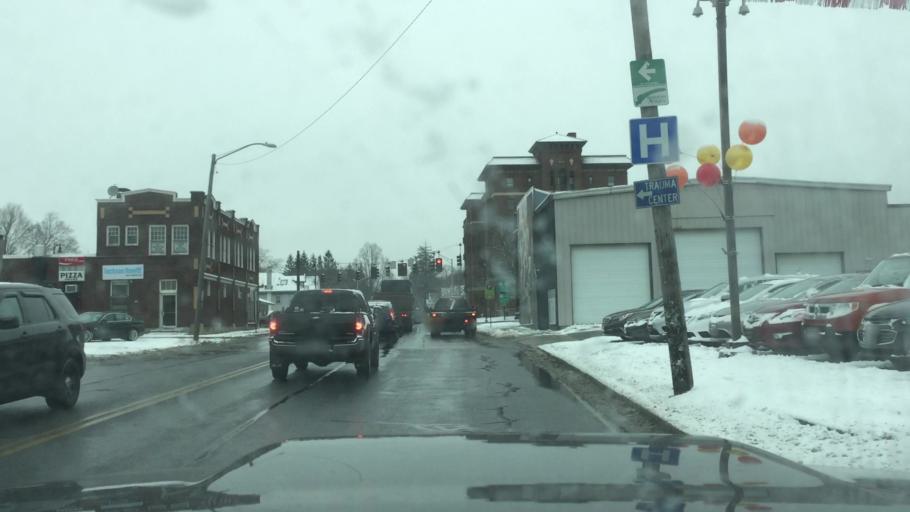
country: US
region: Massachusetts
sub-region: Berkshire County
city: Pittsfield
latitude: 42.4455
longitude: -73.2559
